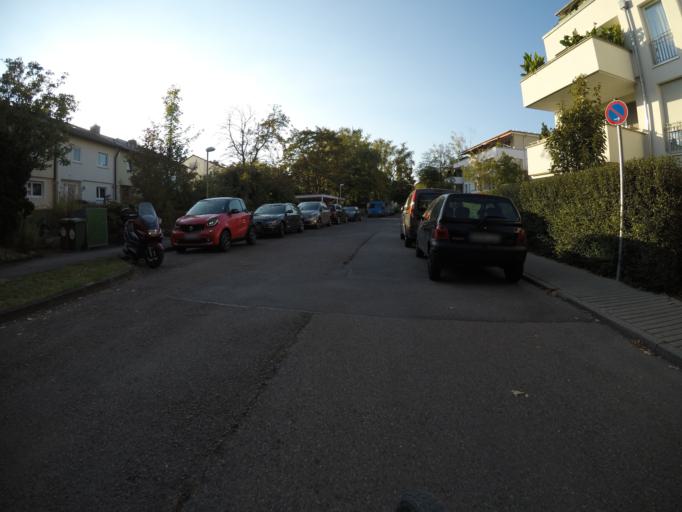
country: DE
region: Baden-Wuerttemberg
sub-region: Regierungsbezirk Stuttgart
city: Ostfildern
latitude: 48.7389
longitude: 9.2325
